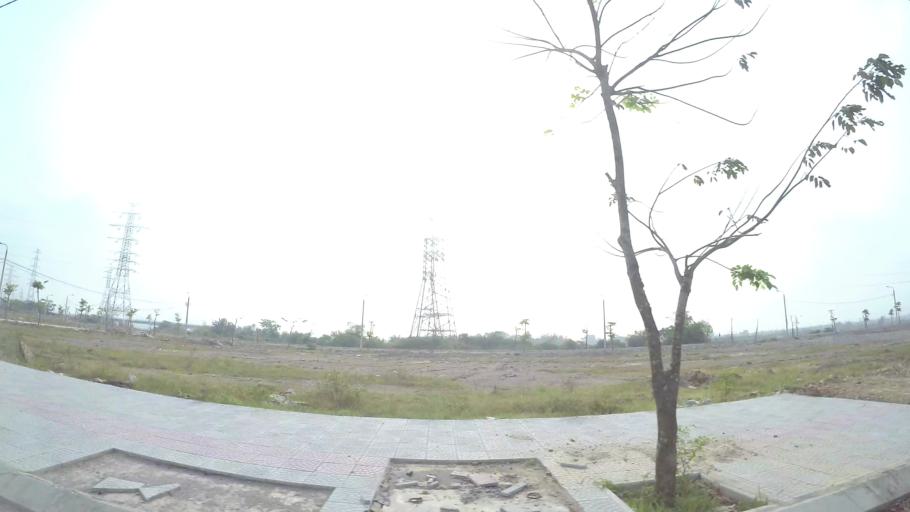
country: VN
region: Da Nang
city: Ngu Hanh Son
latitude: 16.0137
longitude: 108.2313
